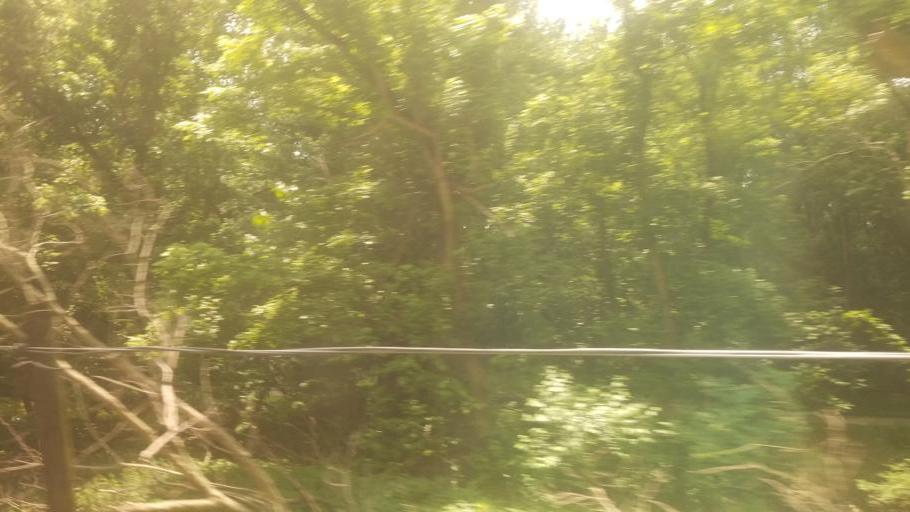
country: US
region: Maryland
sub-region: Frederick County
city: Point of Rocks
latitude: 39.2822
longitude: -77.5478
